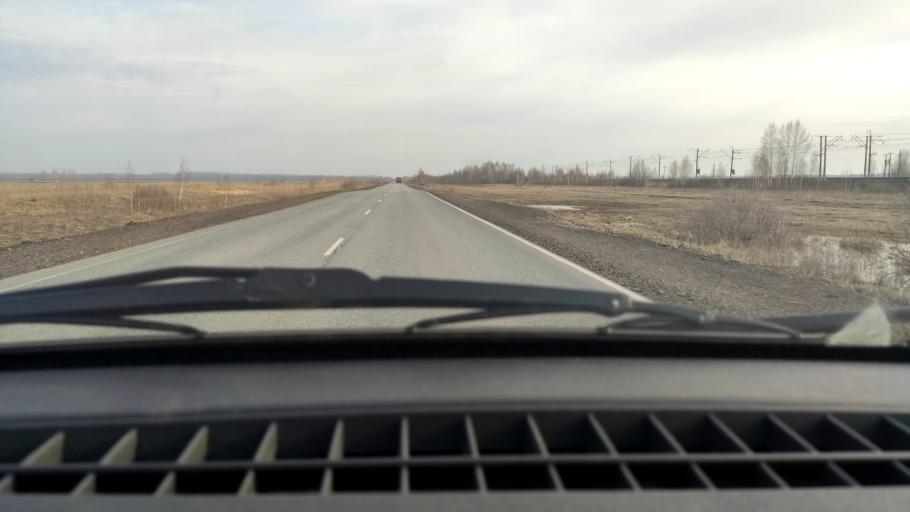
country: RU
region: Bashkortostan
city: Chishmy
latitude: 54.4211
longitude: 55.2285
